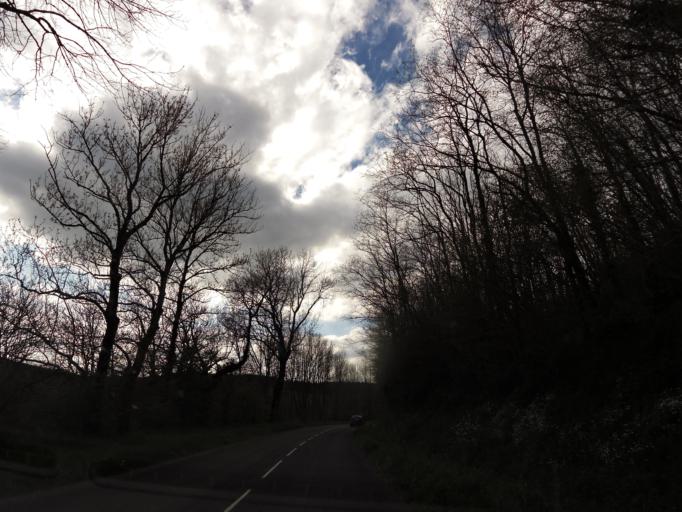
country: FR
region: Midi-Pyrenees
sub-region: Departement du Tarn
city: Soreze
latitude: 43.4128
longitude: 2.0659
